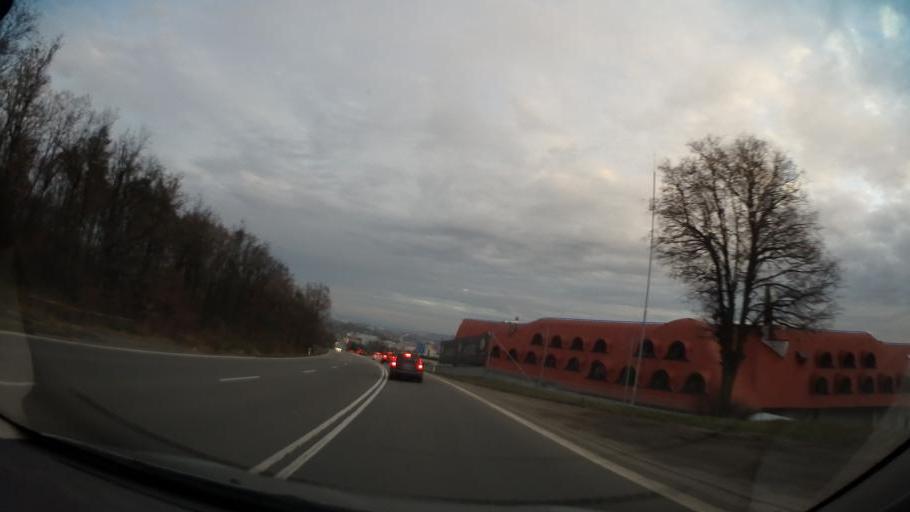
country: CZ
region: South Moravian
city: Troubsko
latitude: 49.1862
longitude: 16.4676
